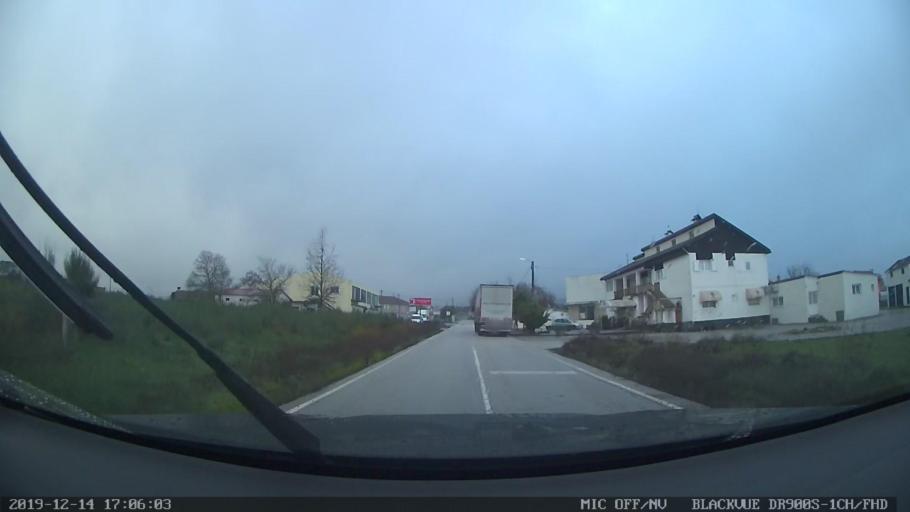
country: PT
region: Vila Real
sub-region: Vila Pouca de Aguiar
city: Vila Pouca de Aguiar
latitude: 41.4543
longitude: -7.5897
